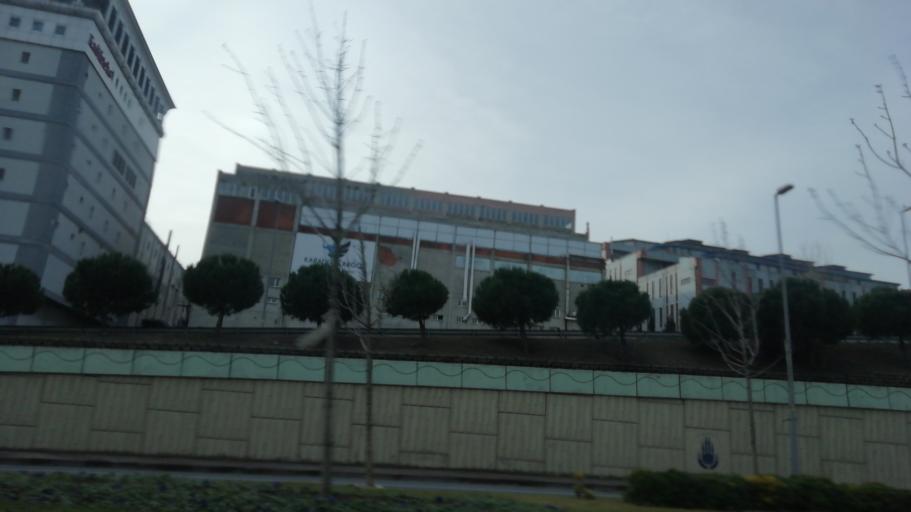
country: TR
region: Istanbul
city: Basaksehir
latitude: 41.0812
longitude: 28.8115
